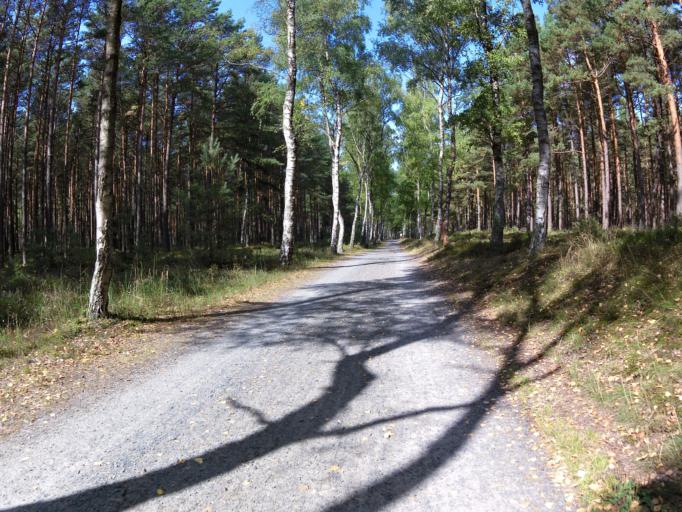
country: DE
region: Mecklenburg-Vorpommern
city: Karlshagen
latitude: 54.0975
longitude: 13.8651
